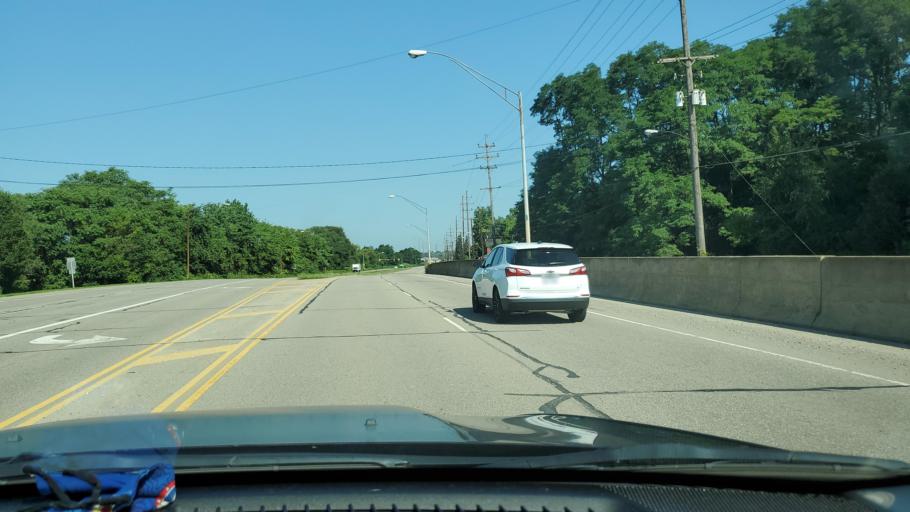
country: US
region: Ohio
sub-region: Trumbull County
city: Girard
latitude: 41.1266
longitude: -80.6799
